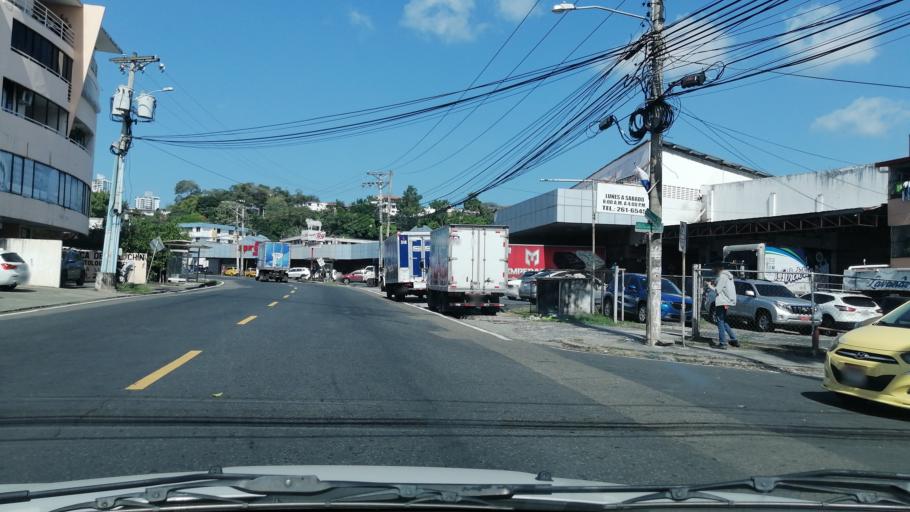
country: PA
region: Panama
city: Panama
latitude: 9.0108
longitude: -79.5244
